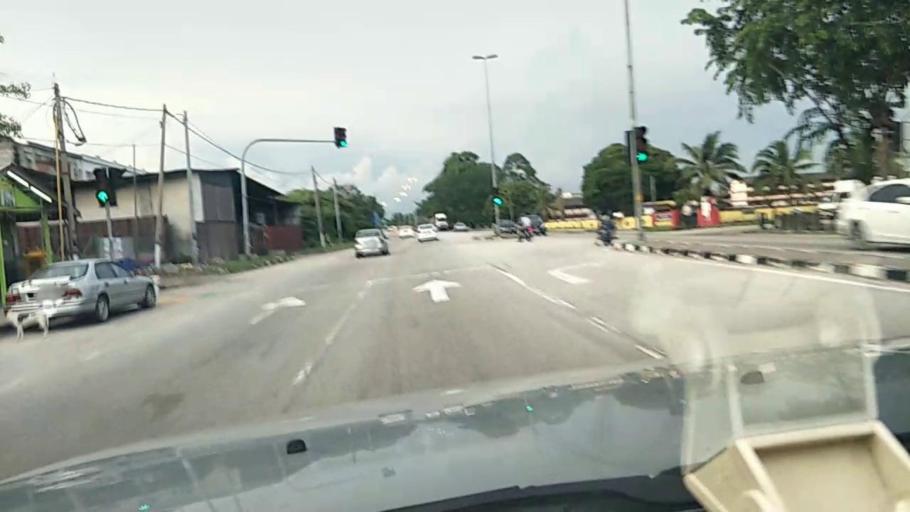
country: MY
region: Perak
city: Kampong Dungun
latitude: 3.1329
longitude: 101.3757
